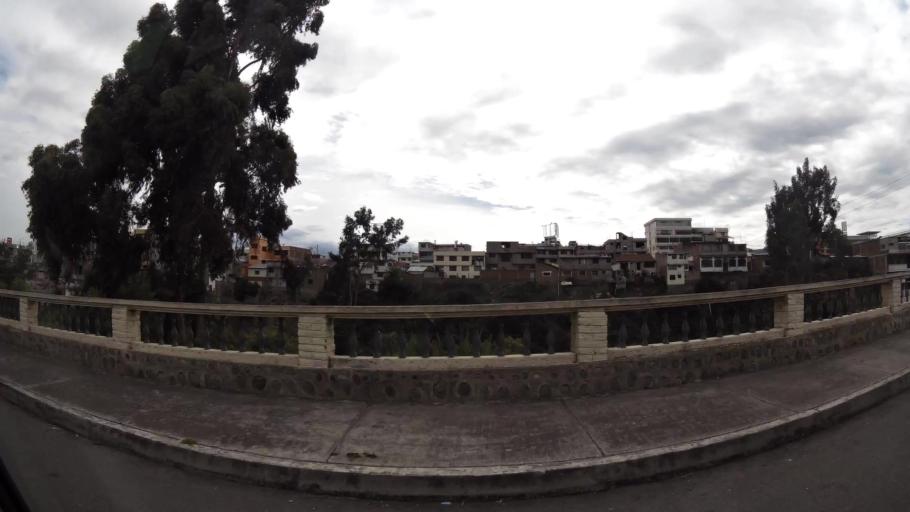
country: EC
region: Cotopaxi
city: Latacunga
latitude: -0.9276
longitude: -78.6233
